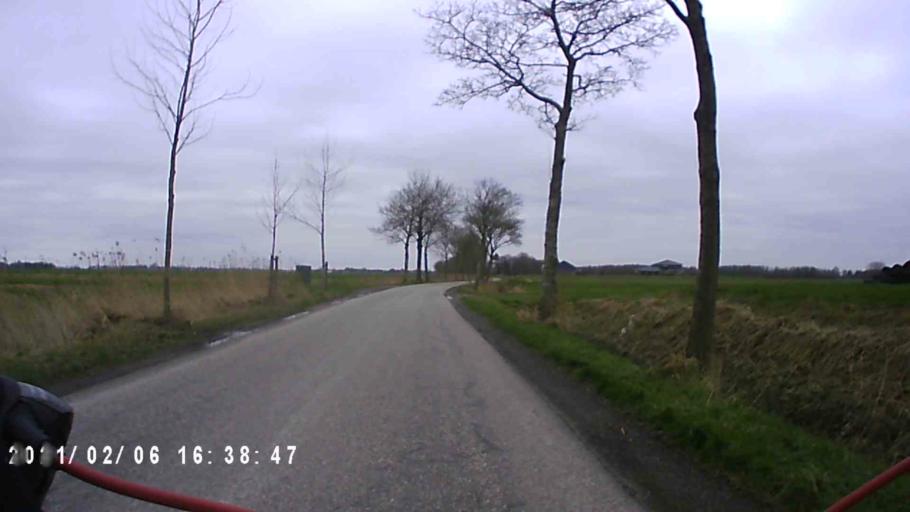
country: NL
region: Groningen
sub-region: Gemeente Bedum
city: Bedum
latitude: 53.4198
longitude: 6.7028
